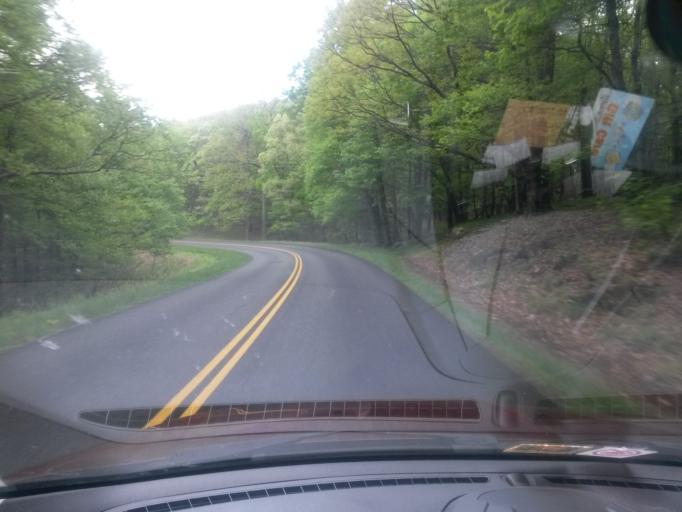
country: US
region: Virginia
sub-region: Floyd County
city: Floyd
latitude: 36.8155
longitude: -80.3454
